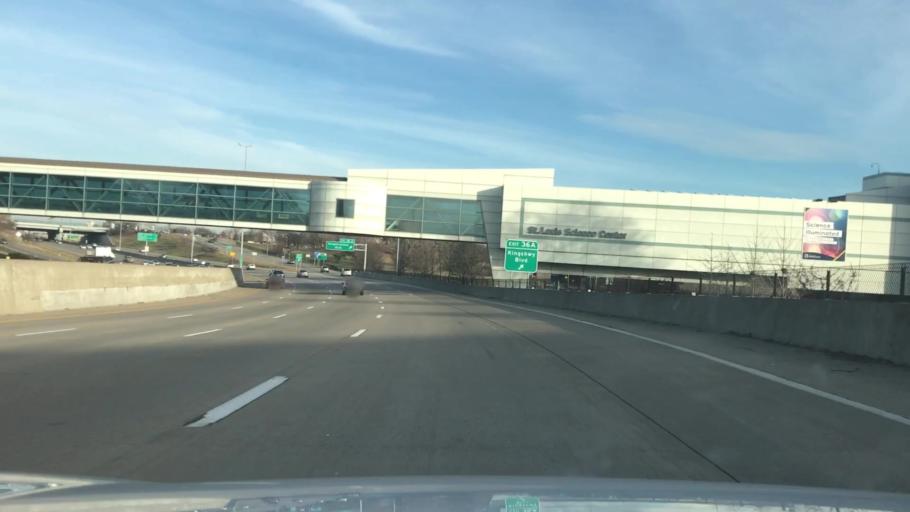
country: US
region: Missouri
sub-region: Saint Louis County
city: University City
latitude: 38.6296
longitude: -90.2715
